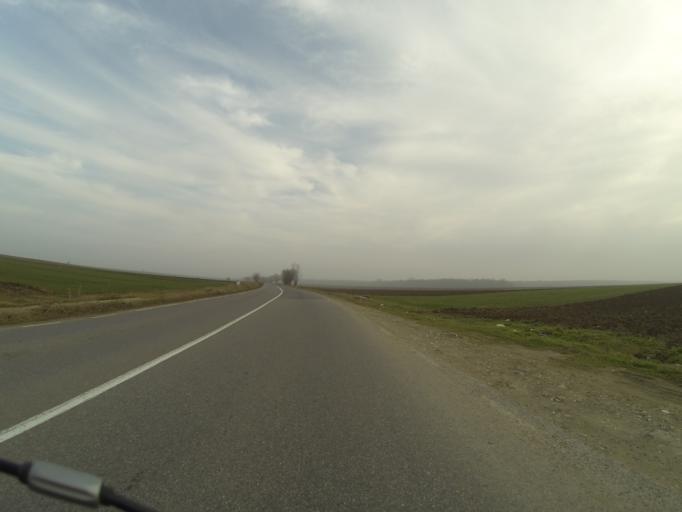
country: RO
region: Mehedinti
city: Vanju-Mare
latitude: 44.4096
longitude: 22.8860
